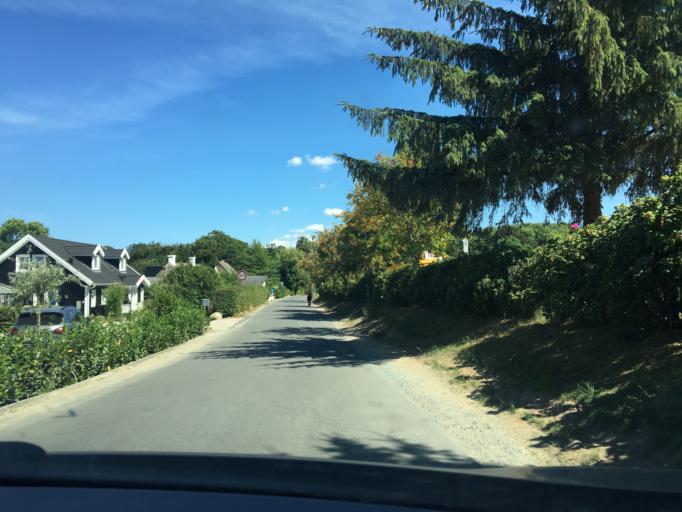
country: DK
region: South Denmark
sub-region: Middelfart Kommune
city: Norre Aby
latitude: 55.5070
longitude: 9.8977
